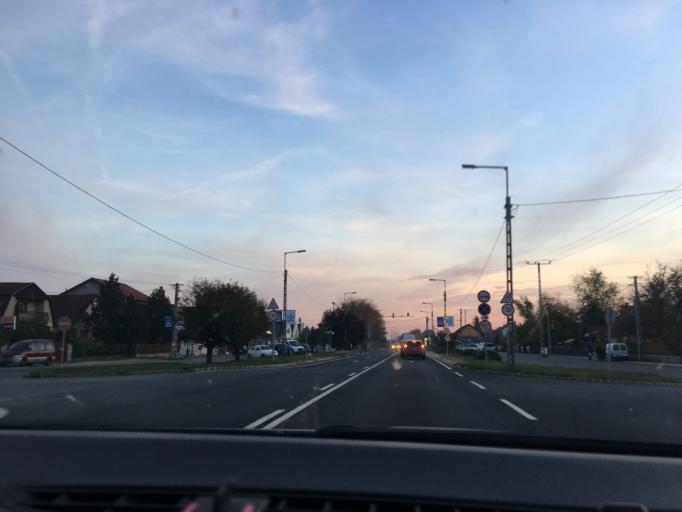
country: HU
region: Hajdu-Bihar
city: Hajduhadhaz
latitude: 47.6446
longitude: 21.6598
